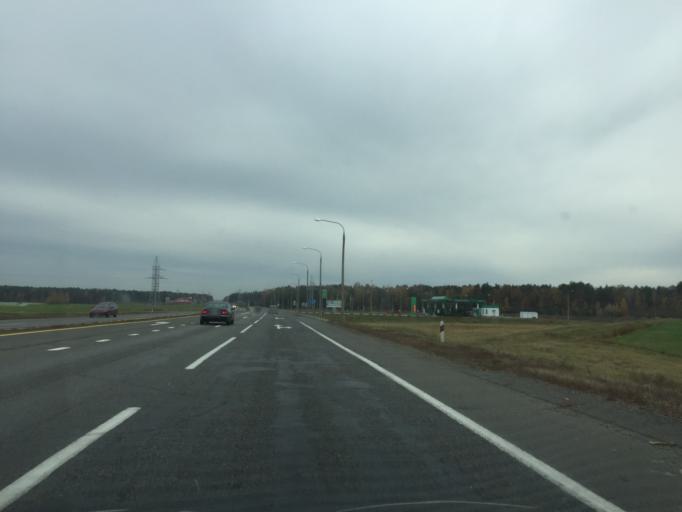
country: BY
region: Gomel
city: Horad Rechytsa
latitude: 52.3397
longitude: 30.5543
